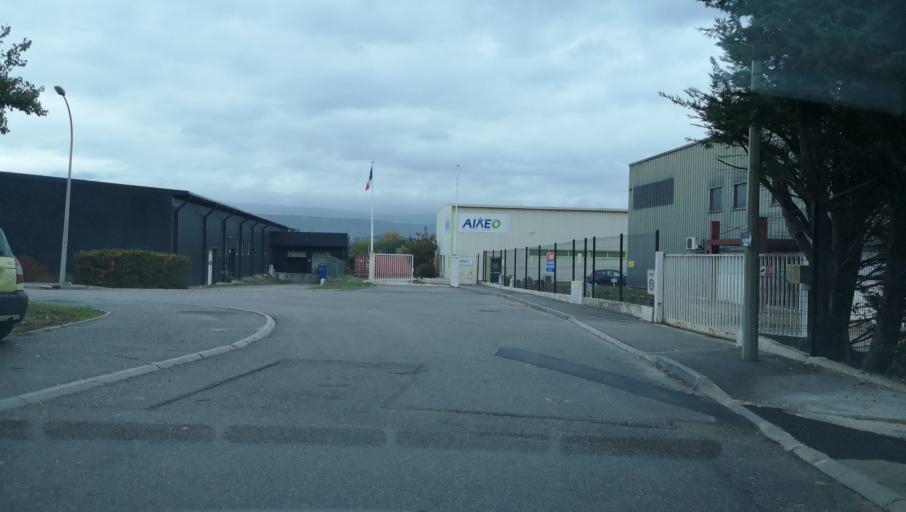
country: FR
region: Provence-Alpes-Cote d'Azur
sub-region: Departement des Bouches-du-Rhone
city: Rousset
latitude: 43.4628
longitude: 5.6215
